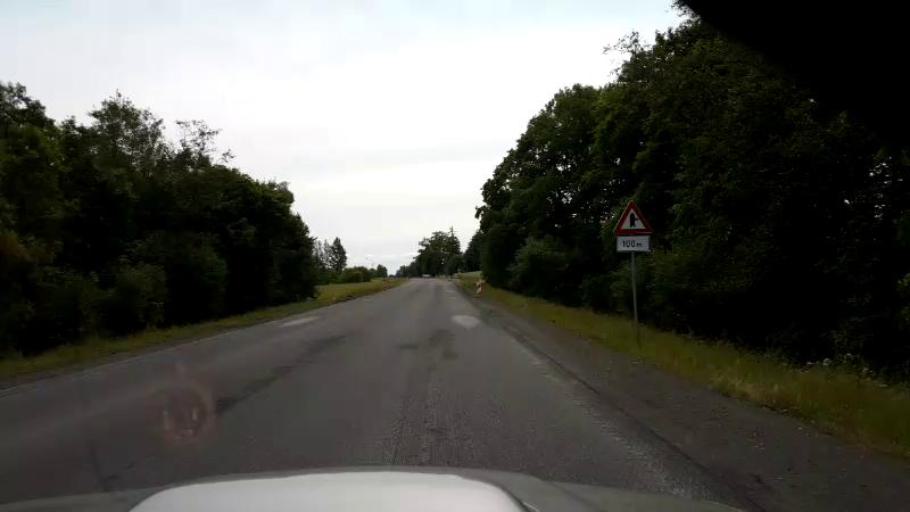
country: LV
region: Bauskas Rajons
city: Bauska
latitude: 56.3245
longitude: 24.3114
